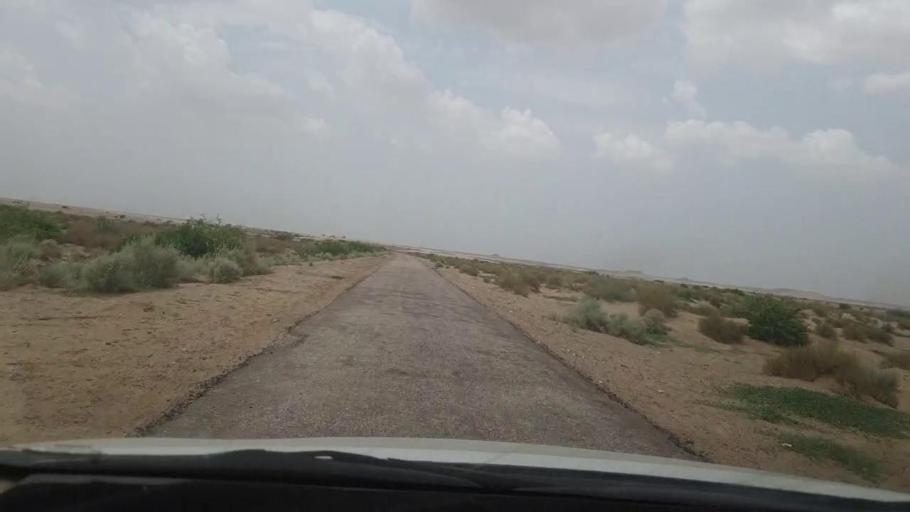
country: PK
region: Sindh
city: Khairpur
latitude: 27.3978
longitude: 68.9766
